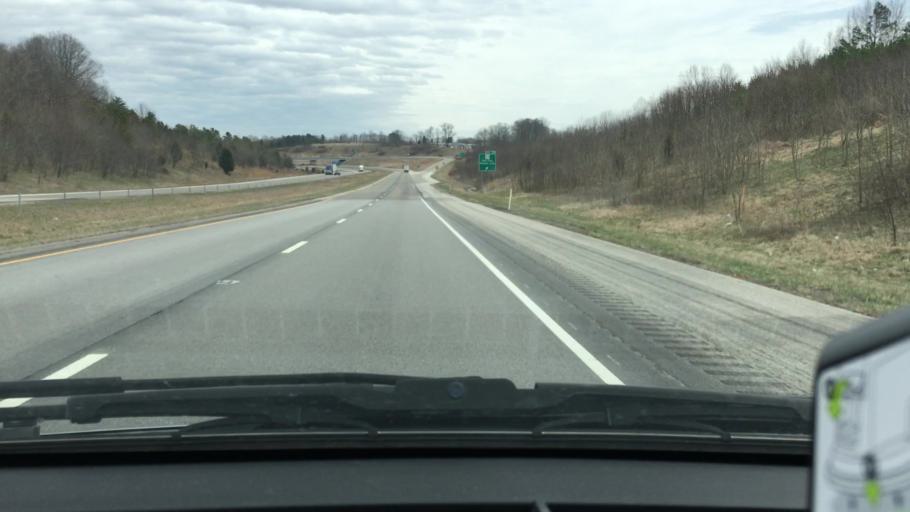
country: US
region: Indiana
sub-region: Crawford County
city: English
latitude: 38.2283
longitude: -86.6016
